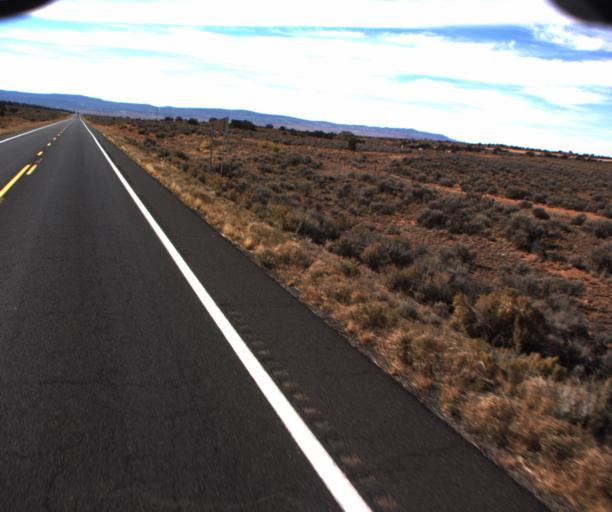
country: US
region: Arizona
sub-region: Coconino County
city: Kaibito
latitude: 36.5427
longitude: -110.7010
